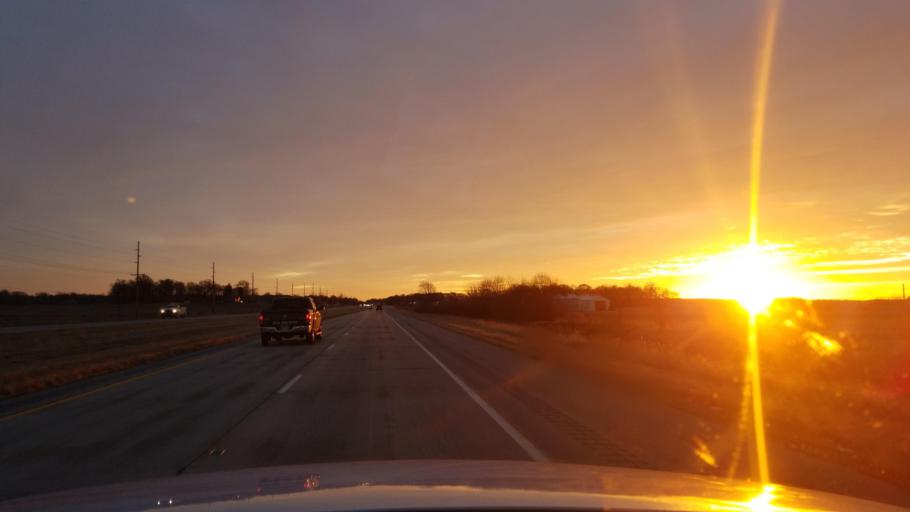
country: US
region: Indiana
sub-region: Posey County
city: Mount Vernon
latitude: 37.9420
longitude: -87.7716
